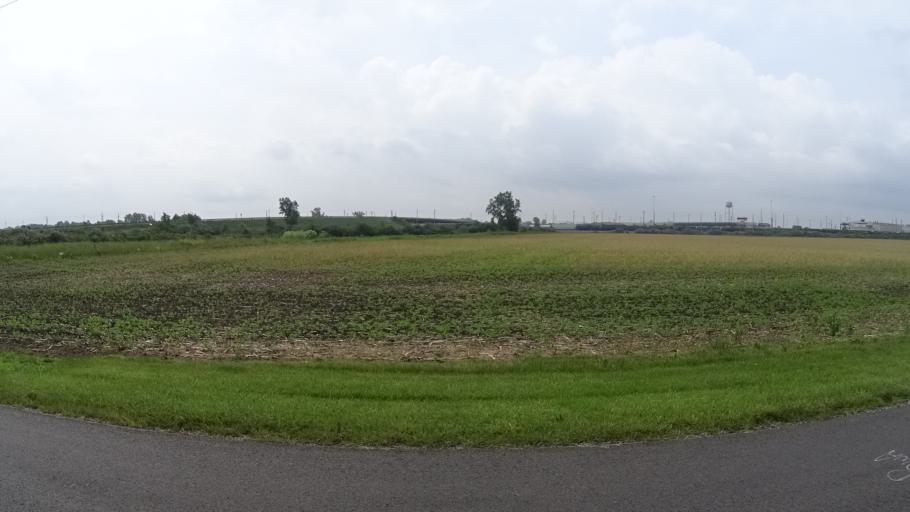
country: US
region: Ohio
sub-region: Huron County
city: Bellevue
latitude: 41.2984
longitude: -82.7814
